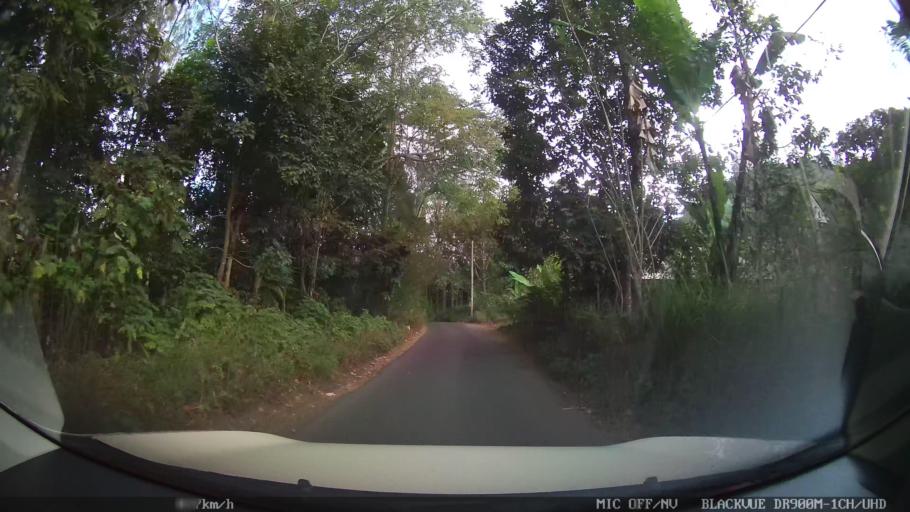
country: ID
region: Bali
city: Banjar Kedisan
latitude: -8.2544
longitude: 115.3493
